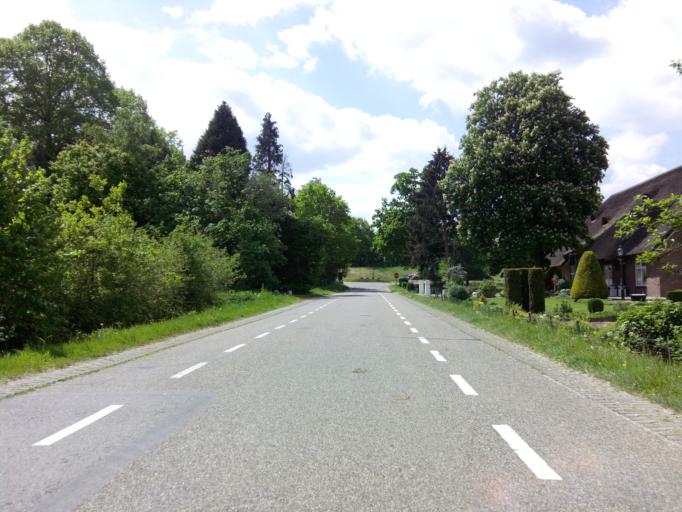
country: NL
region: Utrecht
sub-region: Gemeente Veenendaal
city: Veenendaal
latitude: 52.0518
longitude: 5.5317
